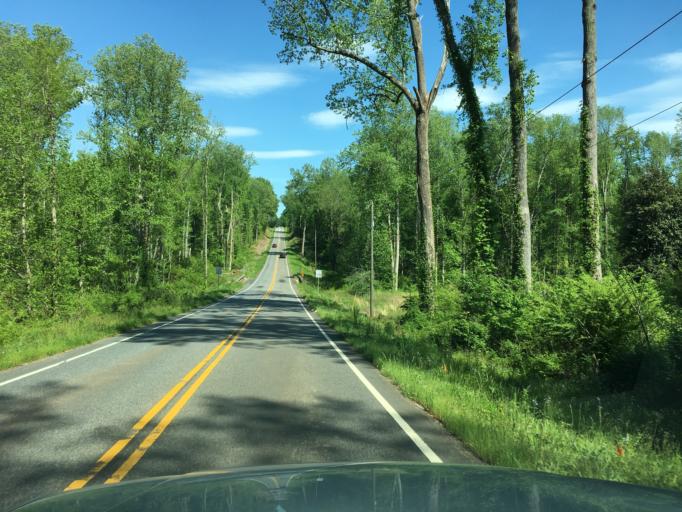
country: US
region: South Carolina
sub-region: Spartanburg County
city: Fairforest
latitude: 34.9703
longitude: -82.0453
